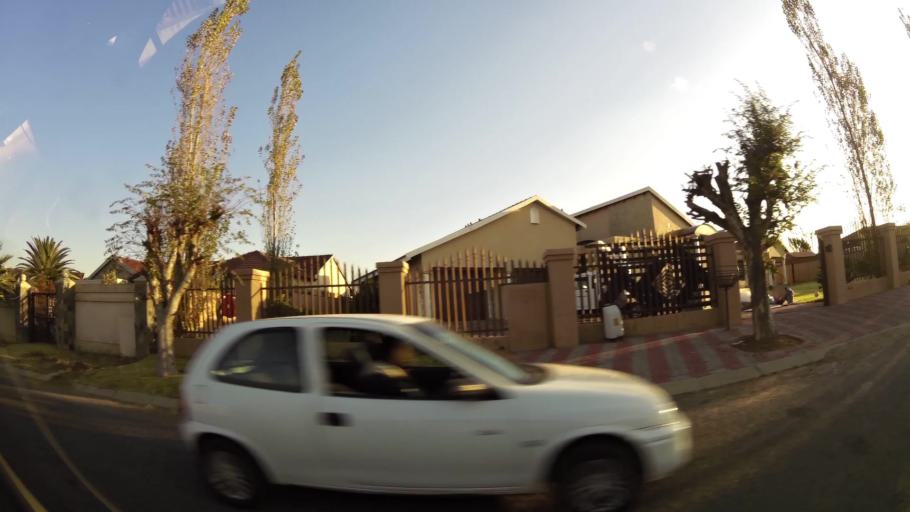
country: ZA
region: Gauteng
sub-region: West Rand District Municipality
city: Randfontein
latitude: -26.2028
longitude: 27.6566
